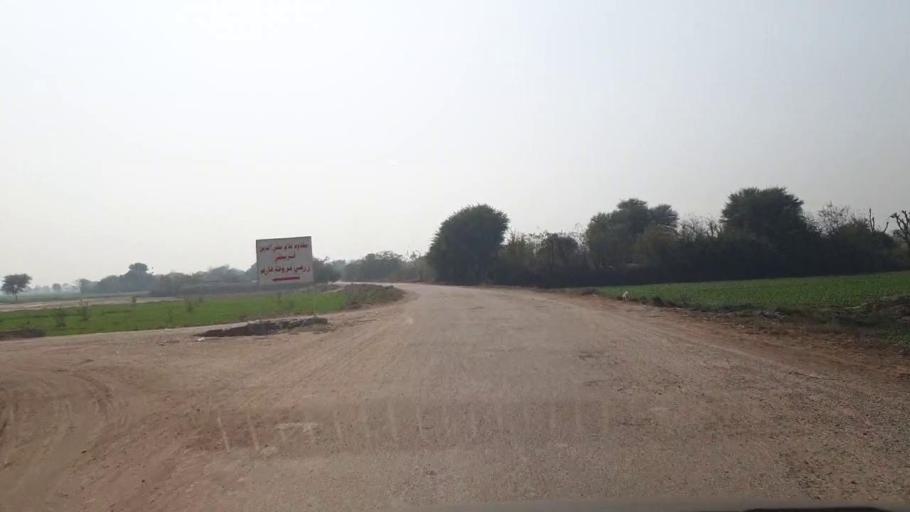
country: PK
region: Sindh
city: Hala
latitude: 25.8955
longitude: 68.4416
